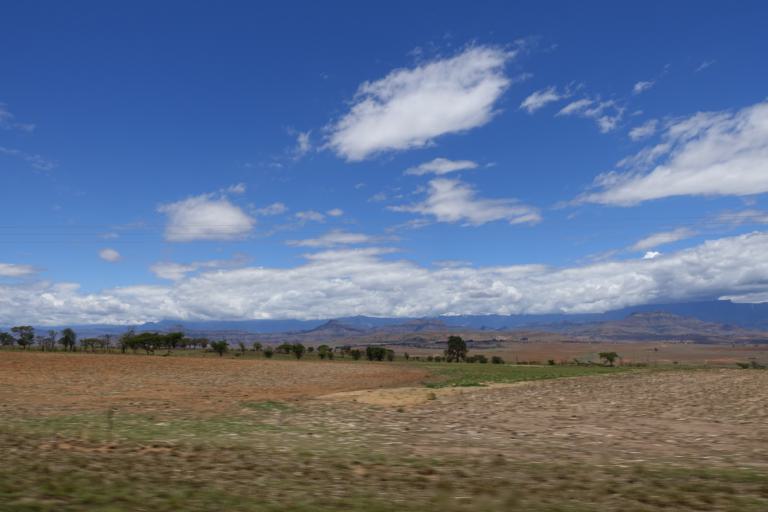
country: ZA
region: KwaZulu-Natal
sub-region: uThukela District Municipality
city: Bergville
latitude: -28.6382
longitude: 29.1485
